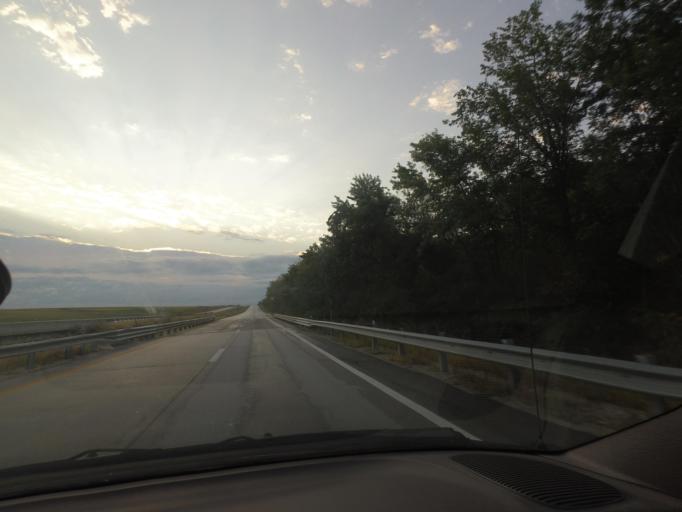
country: US
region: Missouri
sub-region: Shelby County
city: Shelbina
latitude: 39.7232
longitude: -92.1667
